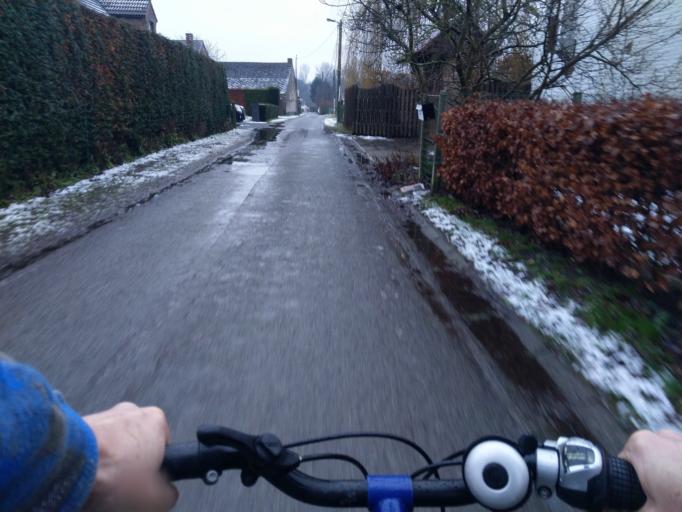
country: BE
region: Wallonia
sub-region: Province du Hainaut
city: Jurbise
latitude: 50.5113
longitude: 3.9466
